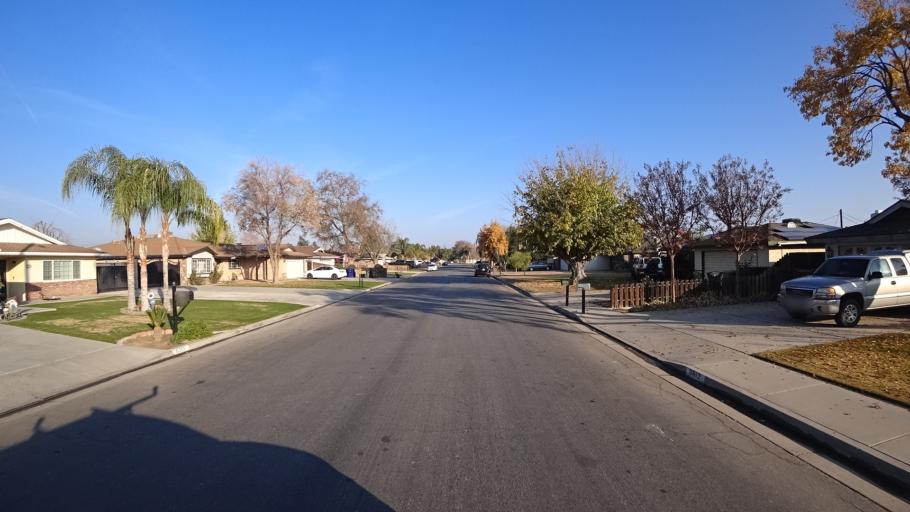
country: US
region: California
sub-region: Kern County
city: Greenfield
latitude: 35.2970
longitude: -119.0199
